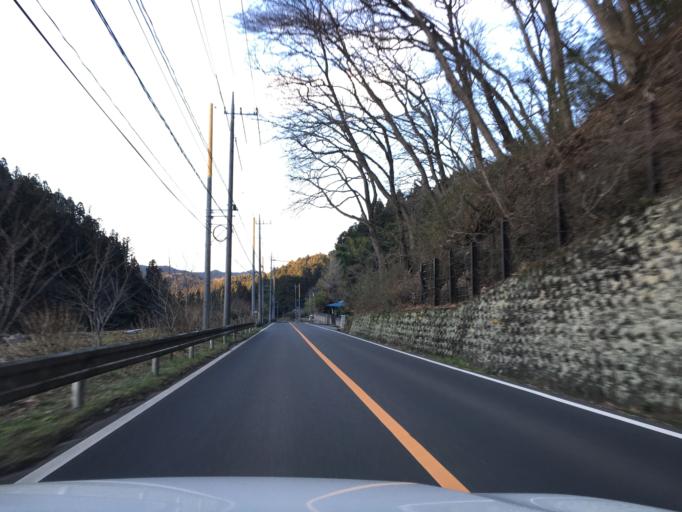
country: JP
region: Tochigi
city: Otawara
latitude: 36.8530
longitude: 140.1752
